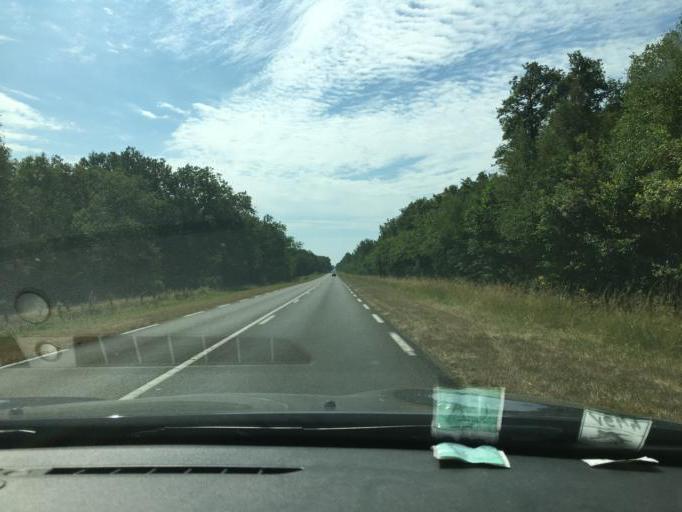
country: FR
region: Centre
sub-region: Departement du Loiret
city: La Ferte-Saint-Aubin
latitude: 47.6843
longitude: 1.9618
